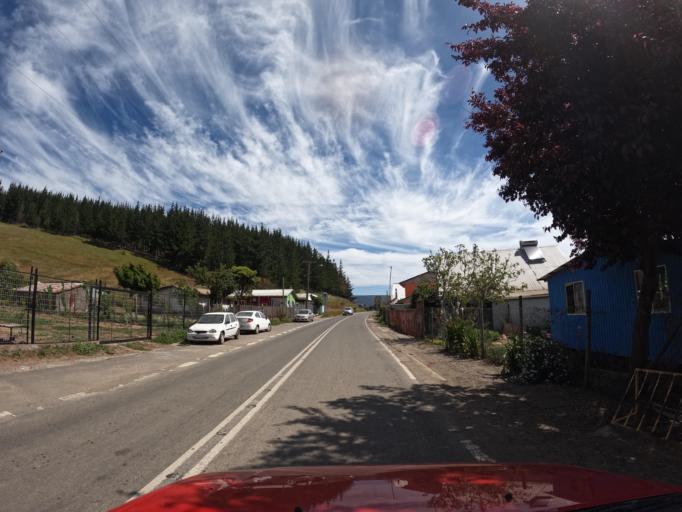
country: CL
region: Maule
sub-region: Provincia de Talca
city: Constitucion
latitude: -35.0233
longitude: -72.0422
